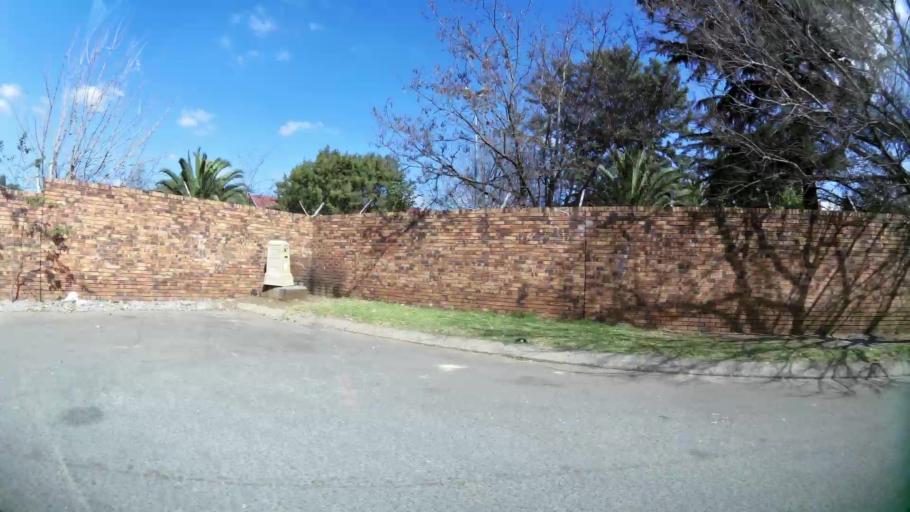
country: ZA
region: Gauteng
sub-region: City of Johannesburg Metropolitan Municipality
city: Soweto
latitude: -26.2467
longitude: 27.8840
